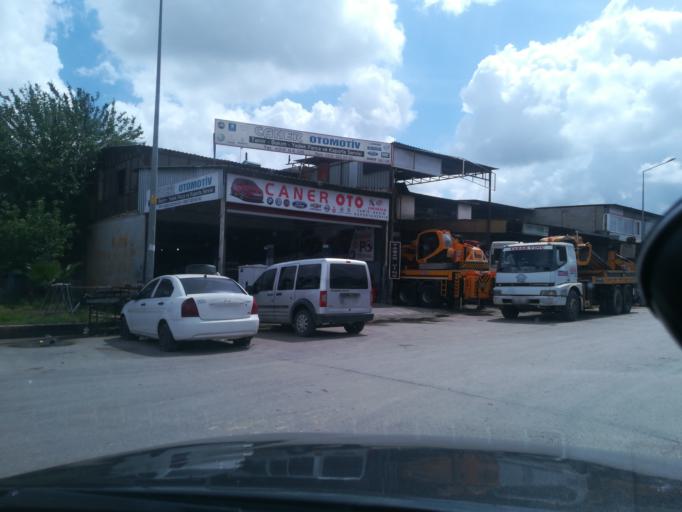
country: TR
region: Adana
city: Seyhan
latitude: 36.9833
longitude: 35.2550
